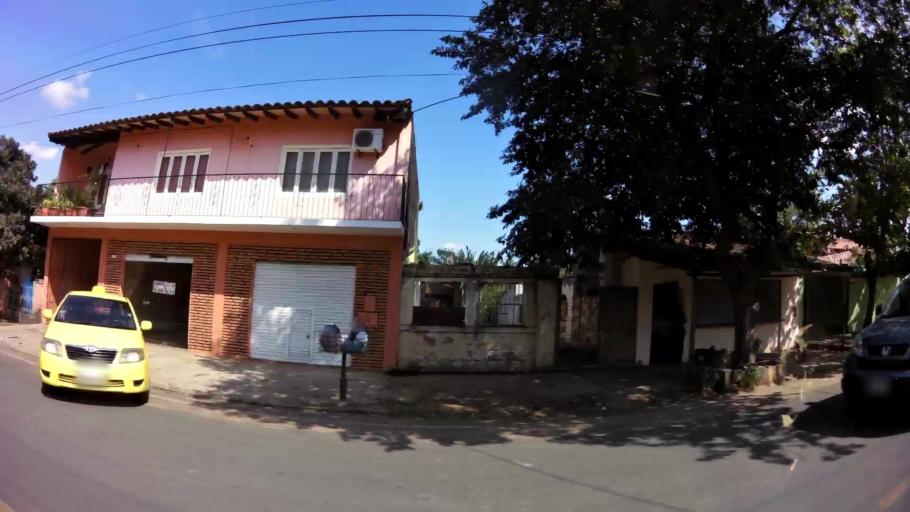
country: PY
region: Central
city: San Lorenzo
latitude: -25.3530
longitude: -57.5087
